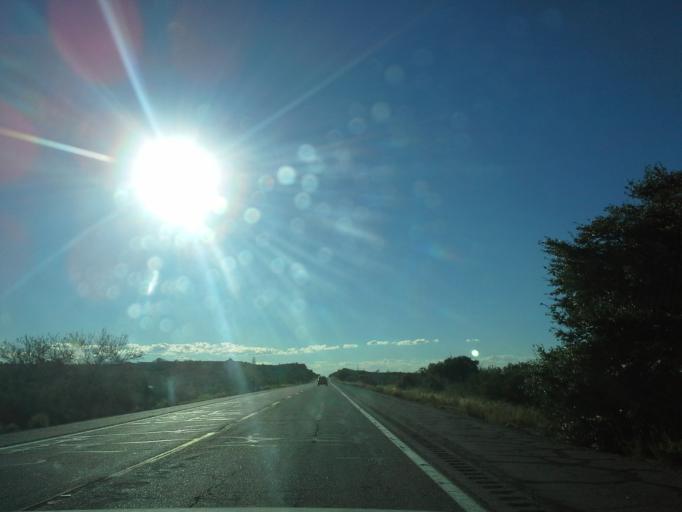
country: US
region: Arizona
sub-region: Pinal County
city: Oracle
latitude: 32.6235
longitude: -110.7631
